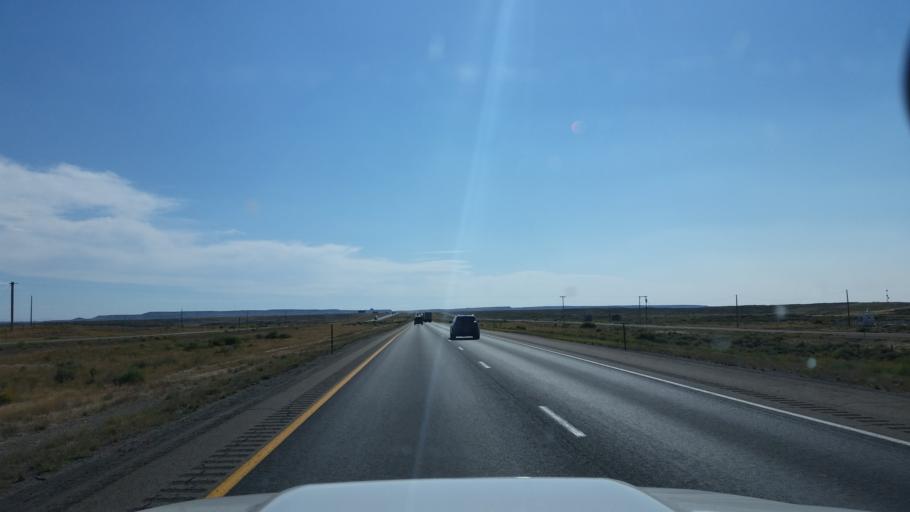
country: US
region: Wyoming
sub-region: Uinta County
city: Lyman
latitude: 41.5330
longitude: -109.9389
